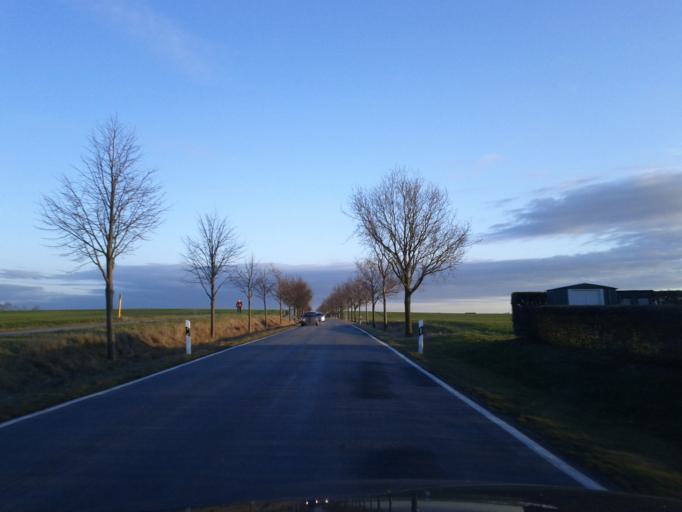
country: DE
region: Mecklenburg-Vorpommern
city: Blowatz
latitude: 53.9833
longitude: 11.4559
